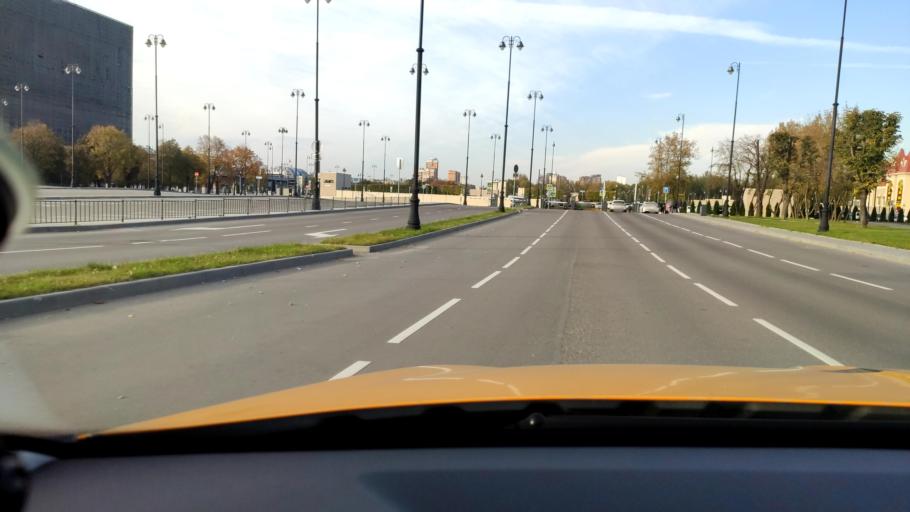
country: RU
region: Moskovskaya
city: Kozhukhovo
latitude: 55.6912
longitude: 37.6695
